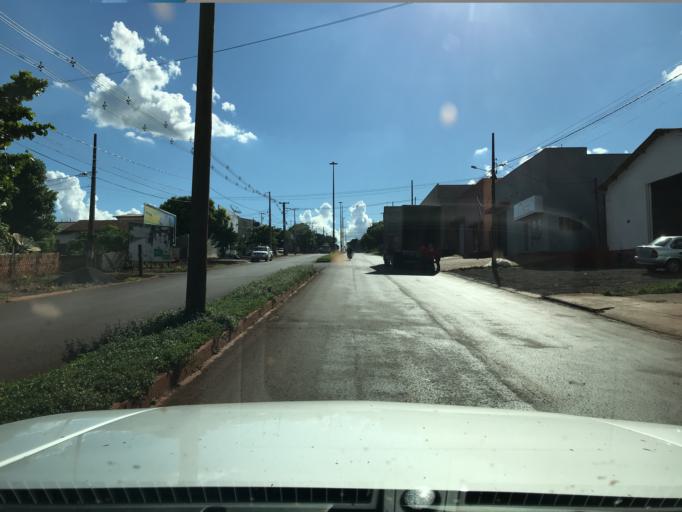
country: BR
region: Parana
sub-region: Palotina
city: Palotina
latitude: -24.2788
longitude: -53.8238
